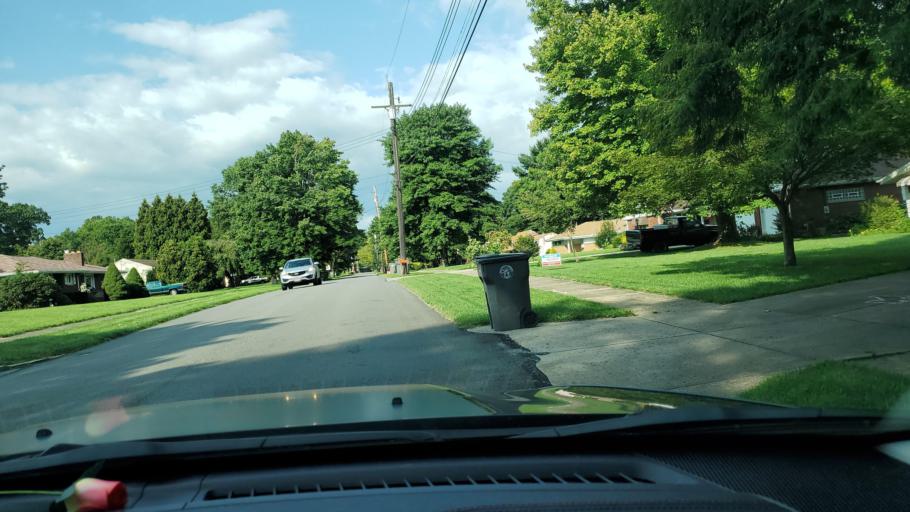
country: US
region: Ohio
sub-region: Mahoning County
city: Youngstown
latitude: 41.0832
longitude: -80.6842
